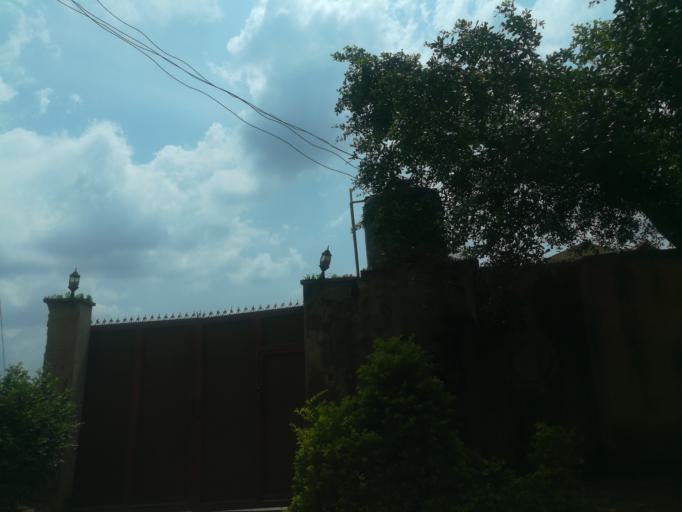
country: NG
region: Oyo
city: Moniya
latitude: 7.4564
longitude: 3.9650
